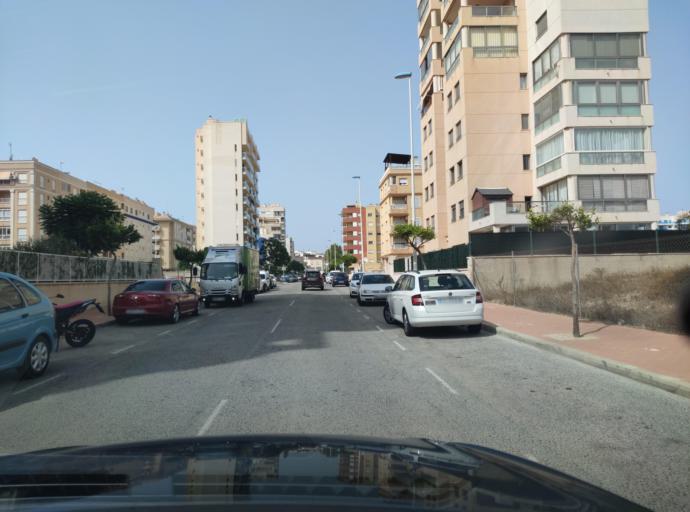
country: ES
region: Valencia
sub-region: Provincia de Alicante
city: Guardamar del Segura
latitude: 38.0973
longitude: -0.6551
